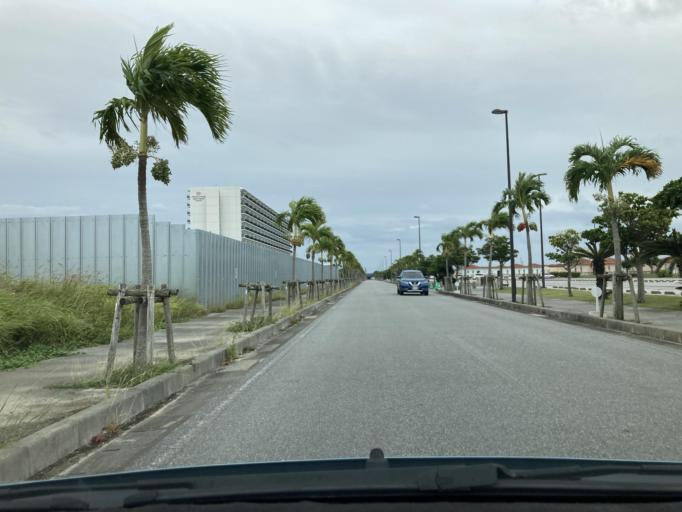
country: JP
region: Okinawa
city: Itoman
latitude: 26.1345
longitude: 127.6516
